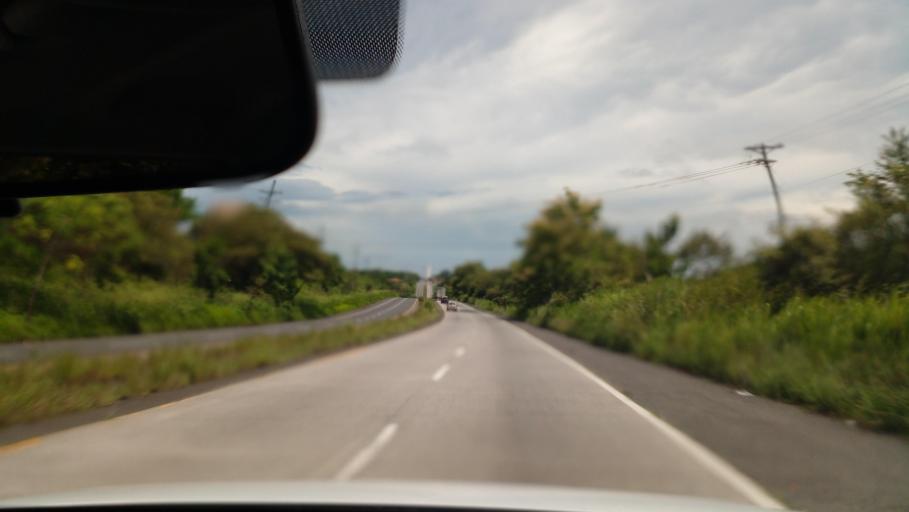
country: PA
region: Panama
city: Nueva Gorgona
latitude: 8.4989
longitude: -79.9582
